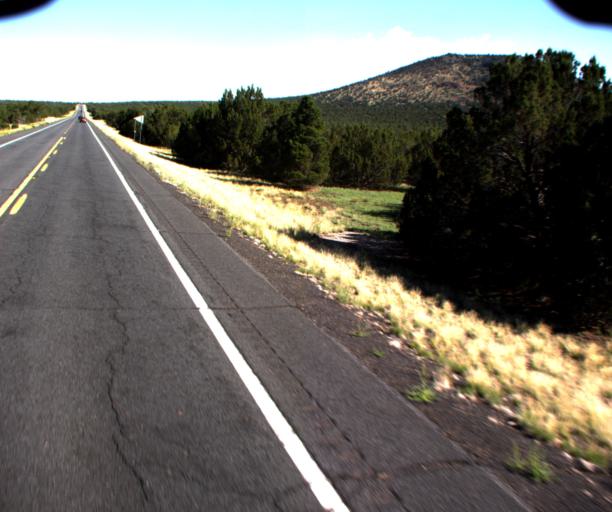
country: US
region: Arizona
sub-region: Coconino County
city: Williams
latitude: 35.3821
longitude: -112.1625
